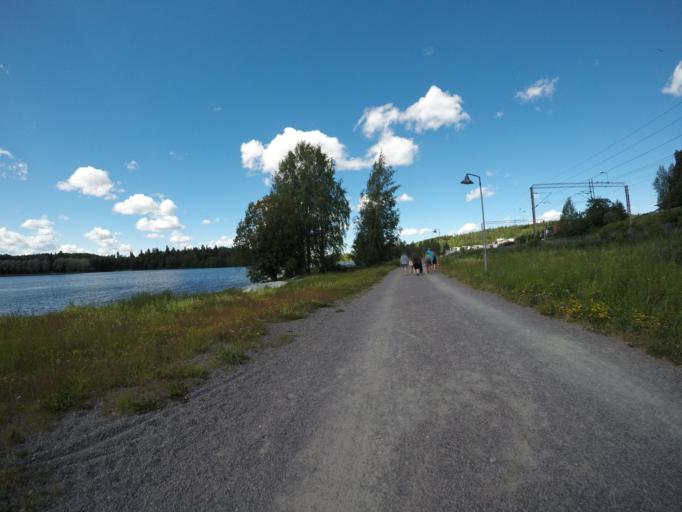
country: FI
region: Haeme
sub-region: Haemeenlinna
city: Haemeenlinna
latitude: 61.0082
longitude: 24.4641
